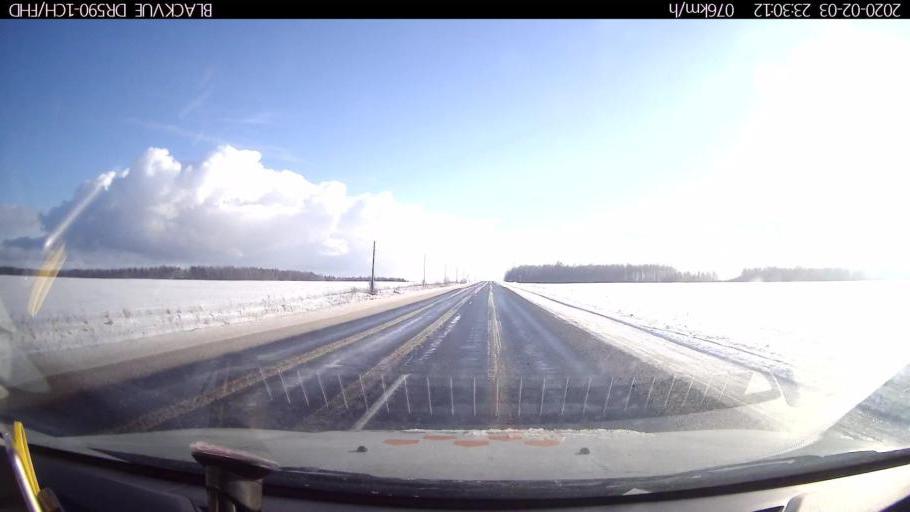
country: RU
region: Nizjnij Novgorod
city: Dal'neye Konstantinovo
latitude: 55.9547
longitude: 44.2129
